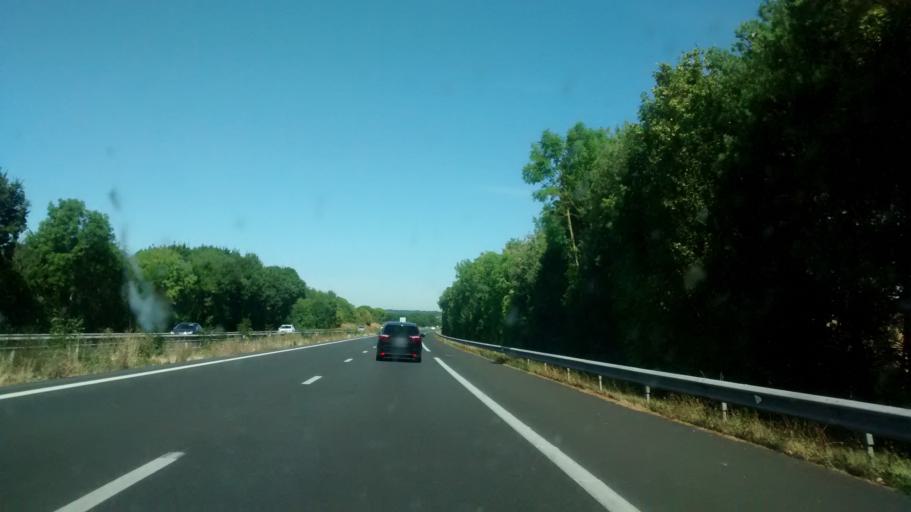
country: FR
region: Poitou-Charentes
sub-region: Departement de la Charente-Maritime
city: Saint-Jean-d'Angely
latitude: 46.0520
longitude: -0.5371
